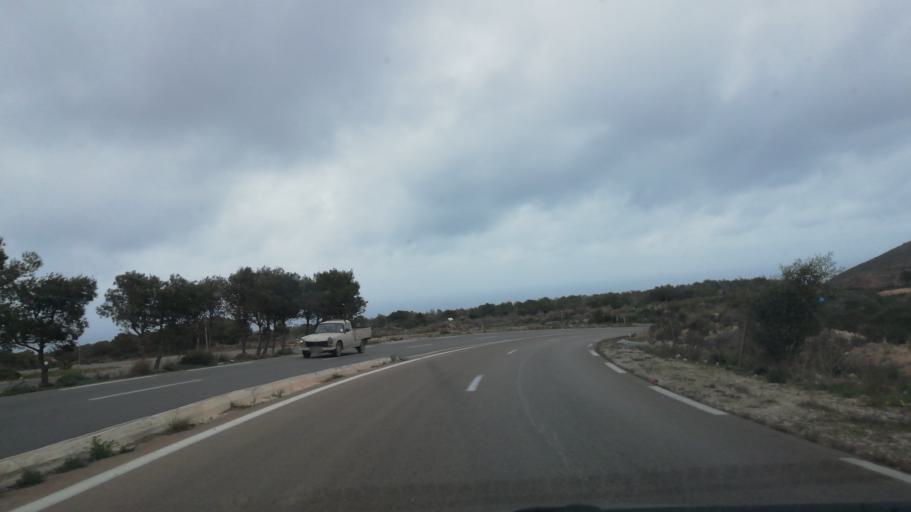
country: DZ
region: Oran
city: Mers el Kebir
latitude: 35.7189
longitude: -0.7416
